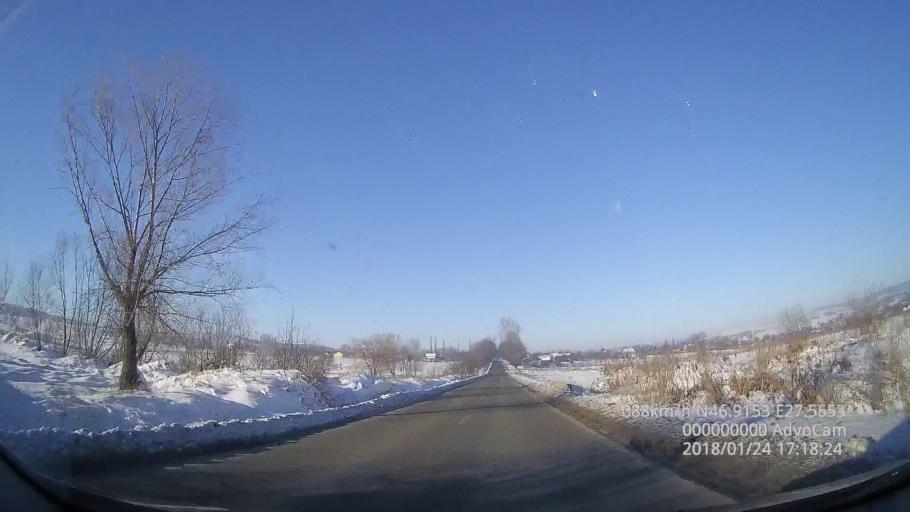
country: RO
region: Iasi
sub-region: Comuna Scanteia
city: Scanteia
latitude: 46.9159
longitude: 27.5652
